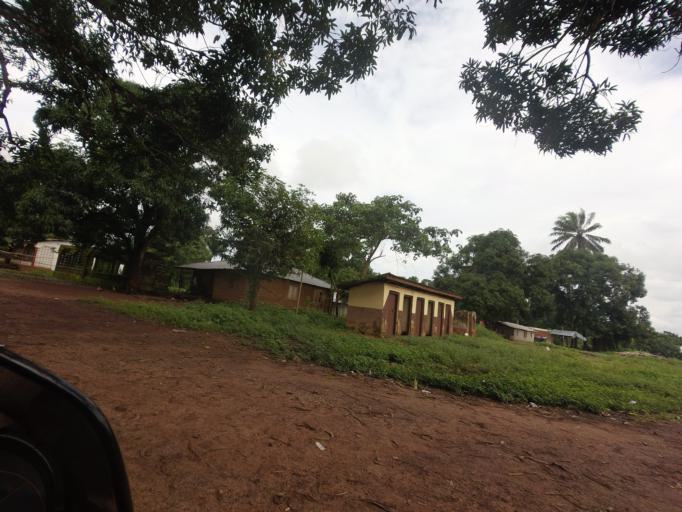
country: SL
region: Northern Province
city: Kambia
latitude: 9.1227
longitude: -12.9160
